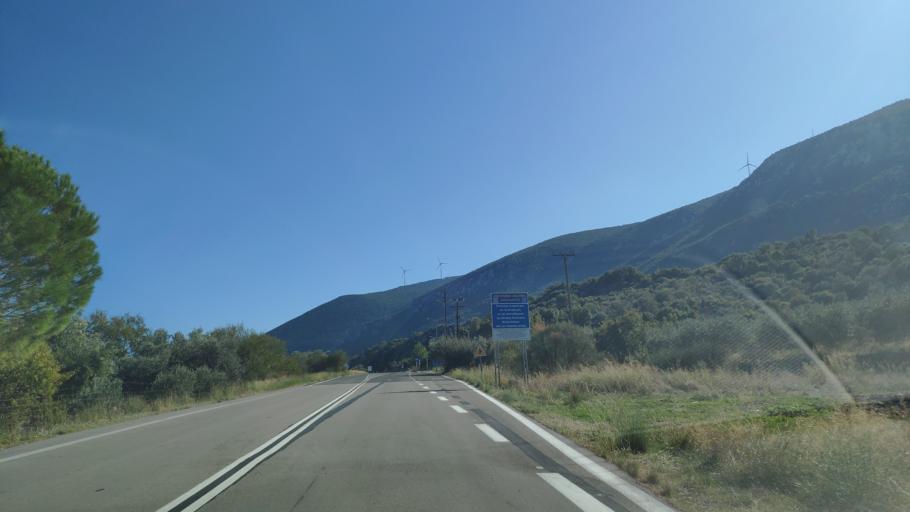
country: GR
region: Peloponnese
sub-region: Nomos Argolidos
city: Palaia Epidavros
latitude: 37.5672
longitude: 23.2520
